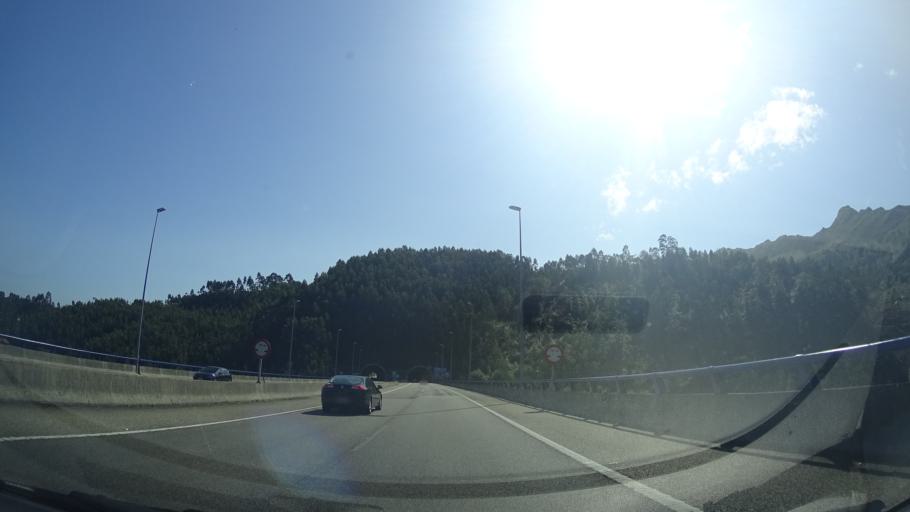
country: ES
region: Asturias
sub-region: Province of Asturias
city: Ribadesella
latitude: 43.4349
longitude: -5.0597
